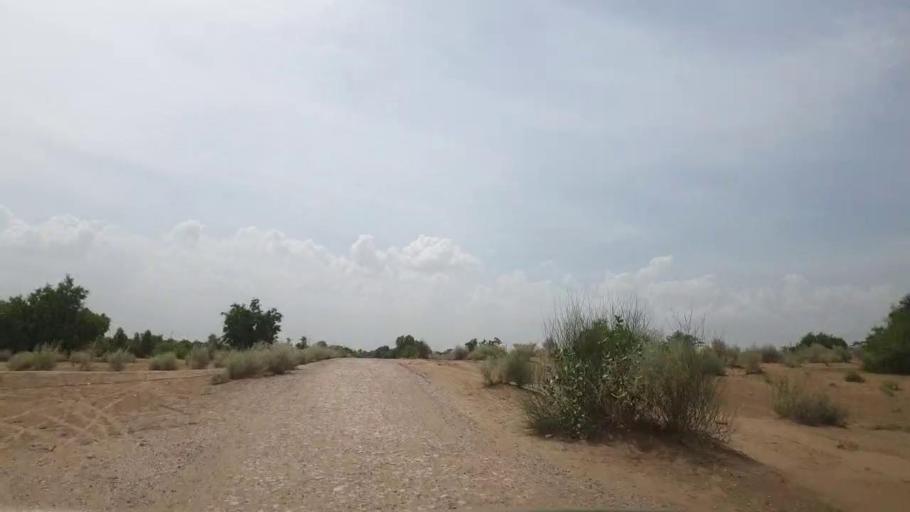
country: PK
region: Sindh
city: Kot Diji
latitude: 27.2533
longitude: 69.0740
